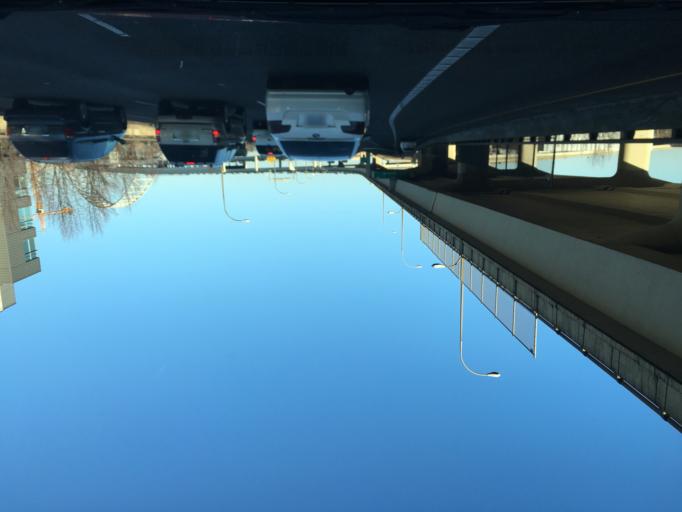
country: US
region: Oregon
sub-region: Multnomah County
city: Portland
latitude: 45.5292
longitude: -122.6872
